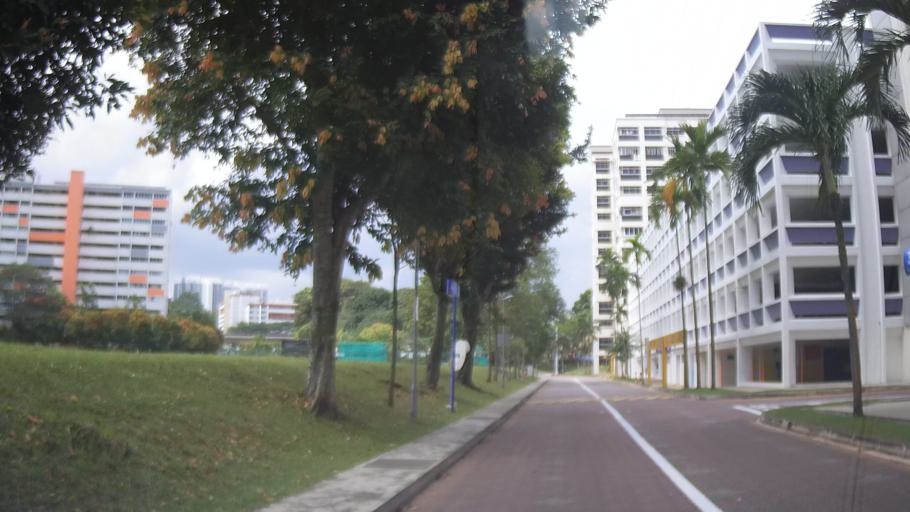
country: MY
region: Johor
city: Johor Bahru
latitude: 1.4326
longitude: 103.7839
